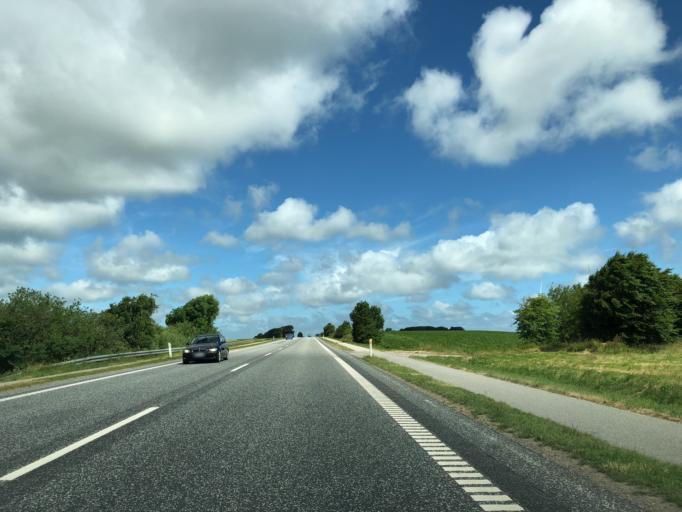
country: DK
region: Central Jutland
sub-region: Holstebro Kommune
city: Holstebro
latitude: 56.4168
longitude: 8.6023
